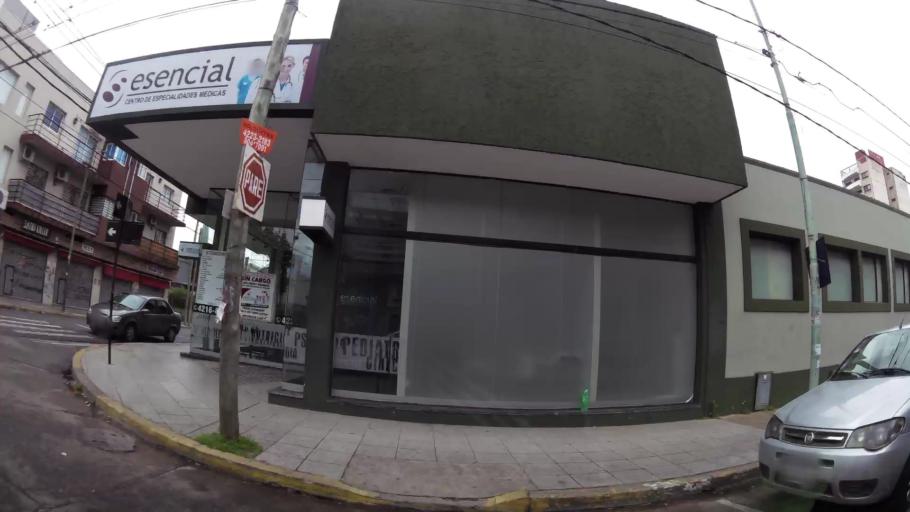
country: AR
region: Buenos Aires
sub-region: Partido de Quilmes
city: Quilmes
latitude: -34.7601
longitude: -58.2090
